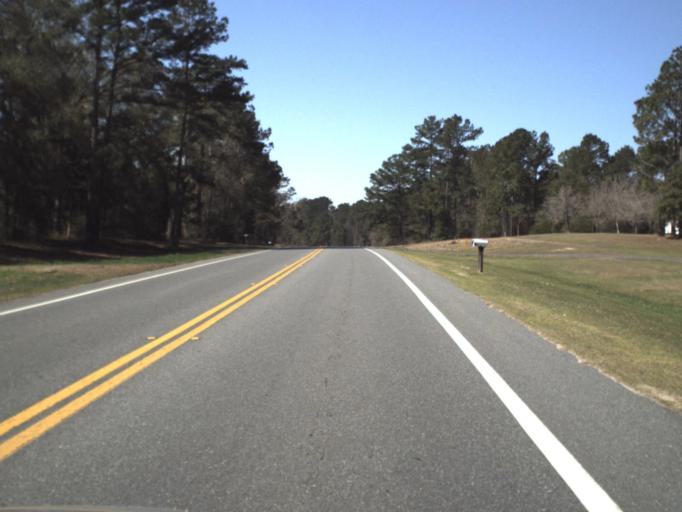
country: US
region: Florida
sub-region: Jackson County
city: Marianna
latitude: 30.7408
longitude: -85.1285
